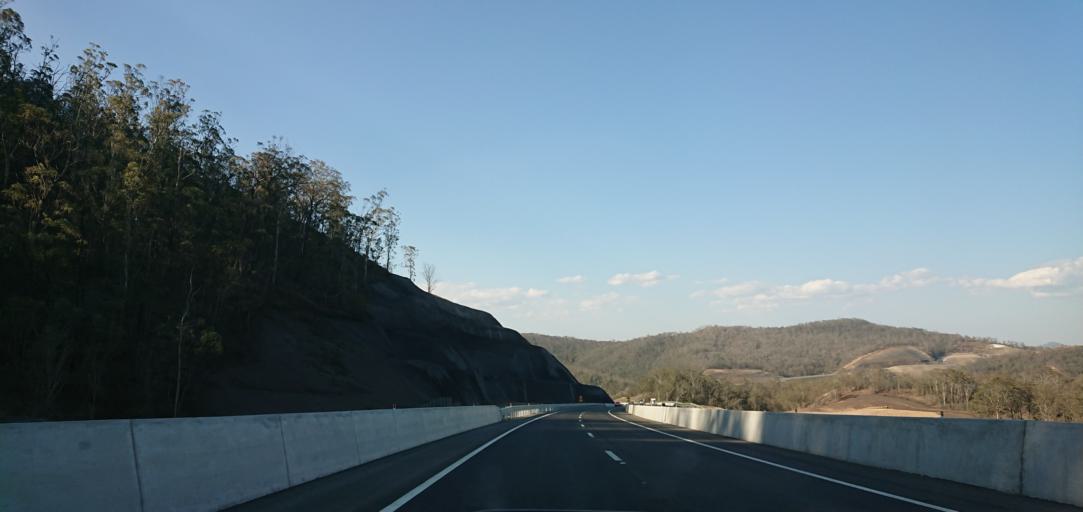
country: AU
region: Queensland
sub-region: Toowoomba
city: Wilsonton Heights
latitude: -27.5093
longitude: 151.9680
